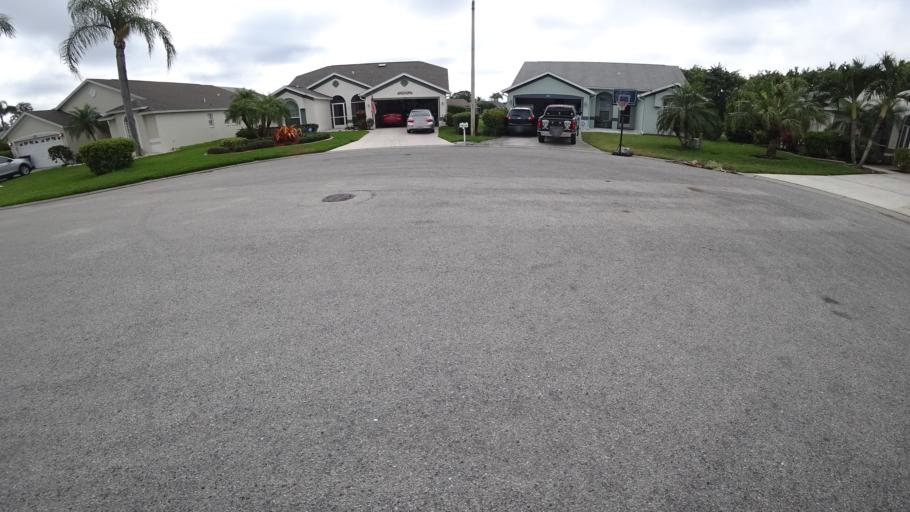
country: US
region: Florida
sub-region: Manatee County
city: South Bradenton
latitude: 27.4507
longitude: -82.6045
